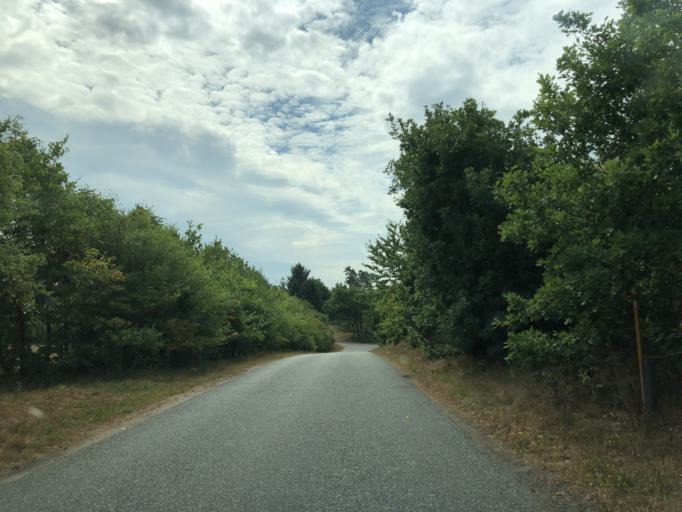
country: DK
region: South Denmark
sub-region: Vejle Kommune
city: Egtved
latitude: 55.6538
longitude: 9.2621
